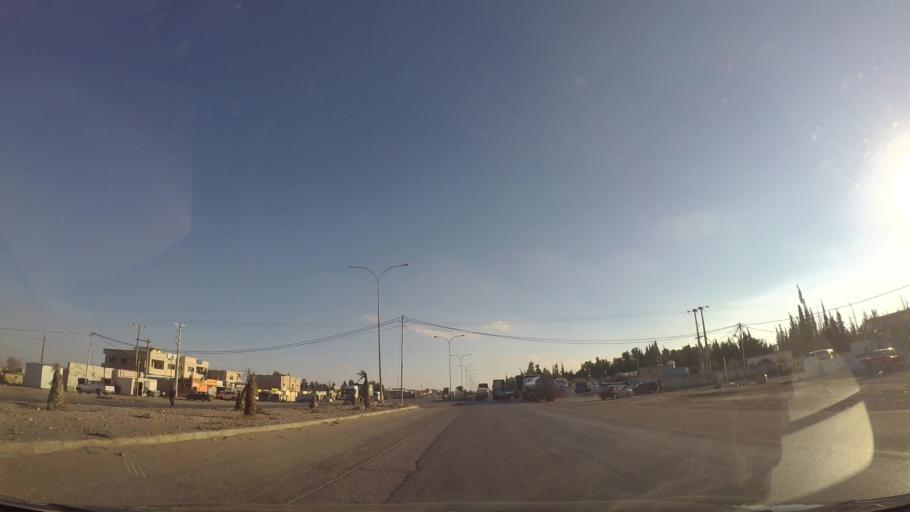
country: JO
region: Tafielah
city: Busayra
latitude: 30.5985
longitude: 35.8044
